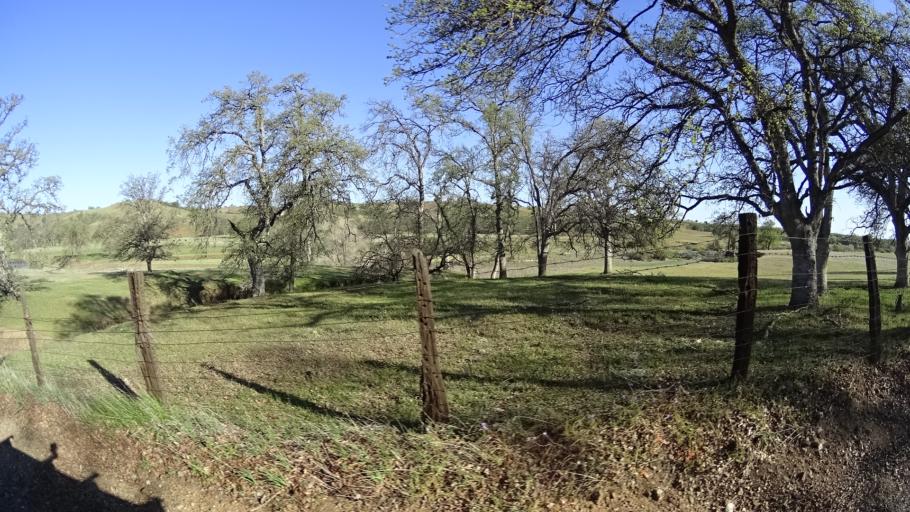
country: US
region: California
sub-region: Tehama County
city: Rancho Tehama Reserve
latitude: 39.7905
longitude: -122.4540
